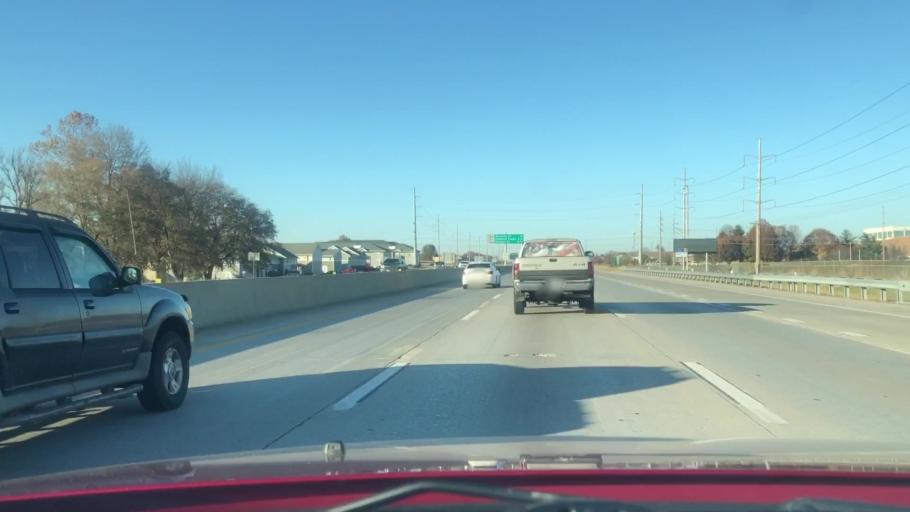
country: US
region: Missouri
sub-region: Greene County
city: Springfield
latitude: 37.1667
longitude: -93.2243
